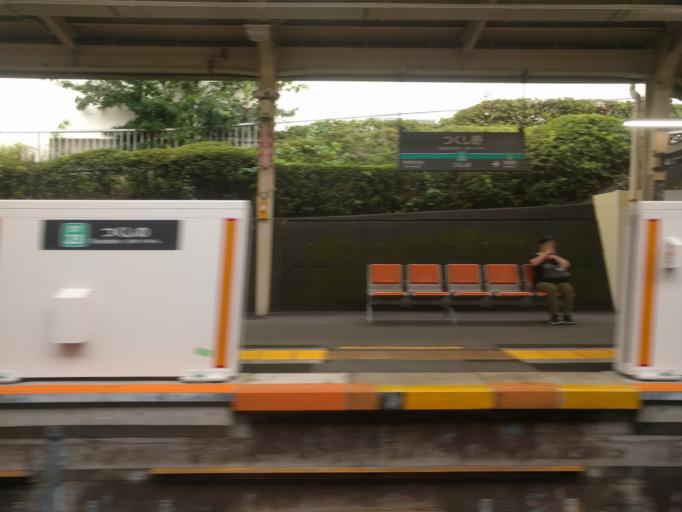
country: JP
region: Tokyo
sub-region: Machida-shi
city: Machida
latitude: 35.5273
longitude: 139.4850
